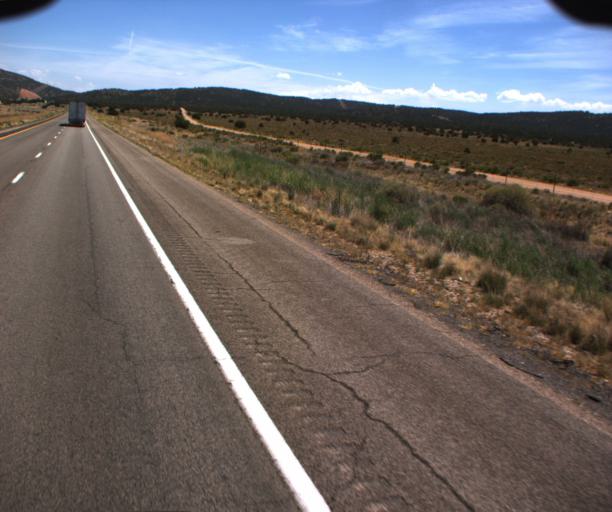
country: US
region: Arizona
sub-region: Mohave County
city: Peach Springs
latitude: 35.2692
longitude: -113.1466
